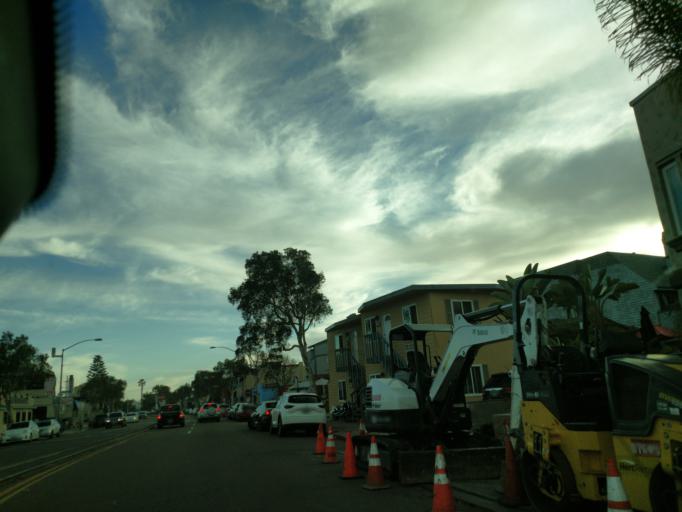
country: US
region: California
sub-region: San Diego County
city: La Jolla
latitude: 32.7663
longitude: -117.2512
